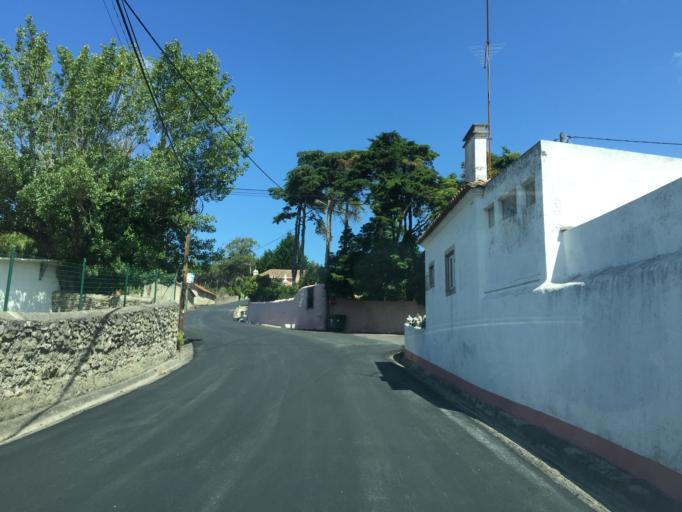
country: PT
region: Lisbon
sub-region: Sintra
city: Sintra
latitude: 38.8112
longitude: -9.4034
